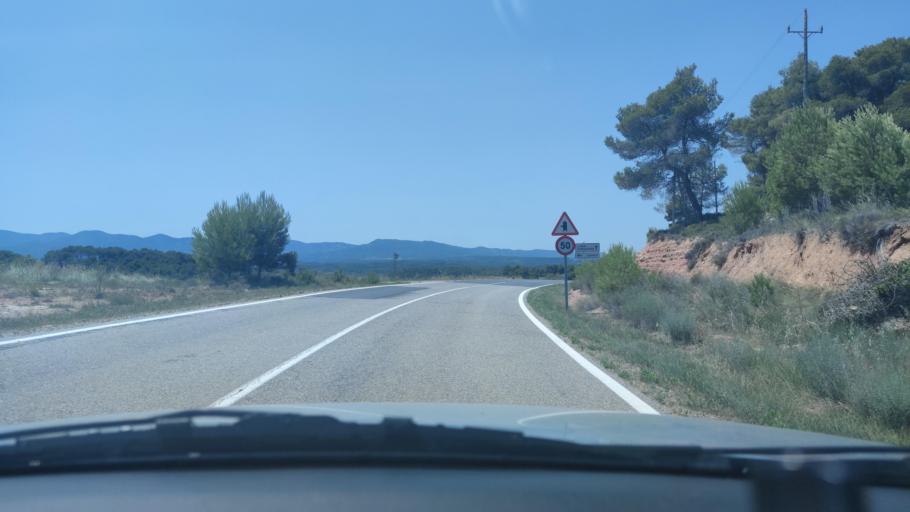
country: ES
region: Catalonia
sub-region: Provincia de Tarragona
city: Vimbodi
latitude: 41.4263
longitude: 1.0291
